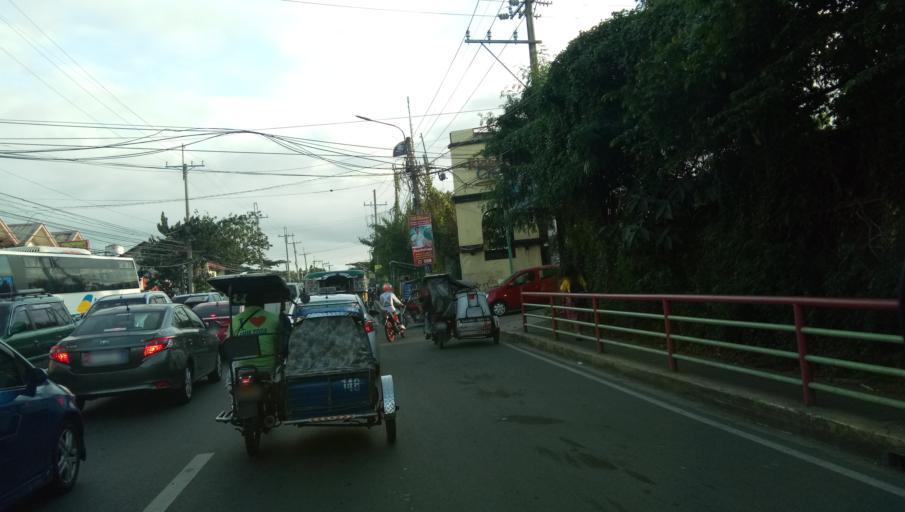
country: PH
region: Calabarzon
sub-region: Province of Cavite
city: Imus
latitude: 14.3825
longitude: 120.9784
